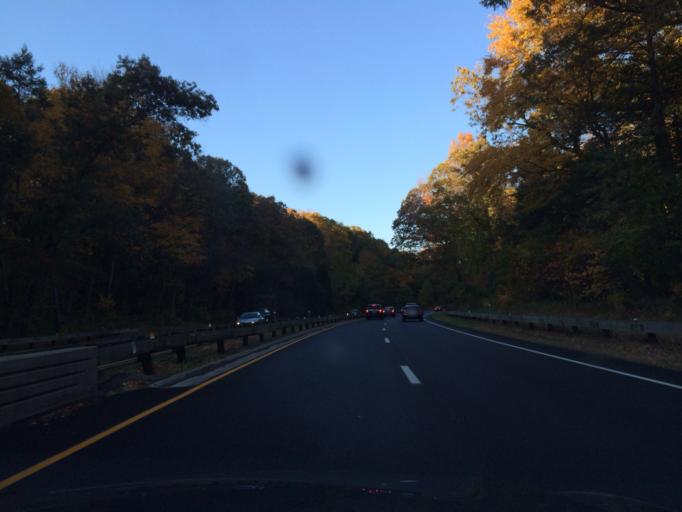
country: US
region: Connecticut
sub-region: Fairfield County
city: Glenville
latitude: 41.0755
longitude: -73.6694
